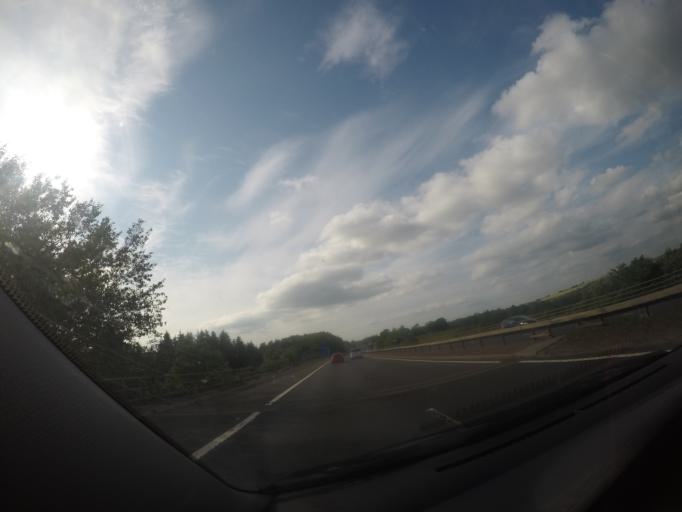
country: GB
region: Scotland
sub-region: South Lanarkshire
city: Lesmahagow
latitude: 55.6448
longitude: -3.8837
